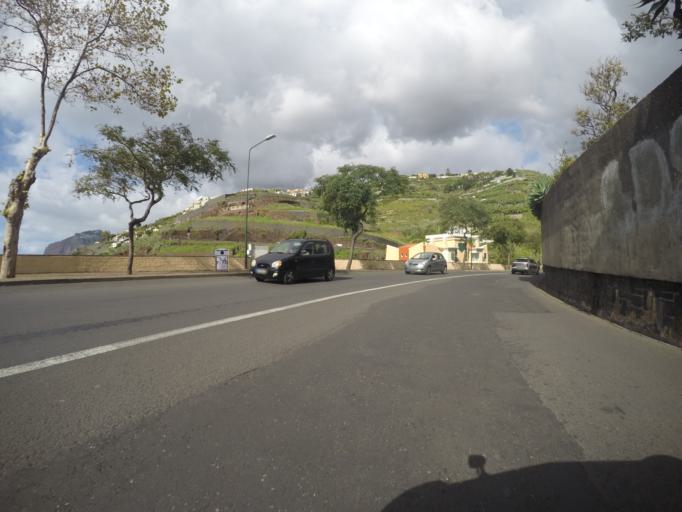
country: PT
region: Madeira
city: Camara de Lobos
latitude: 32.6422
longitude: -16.9505
